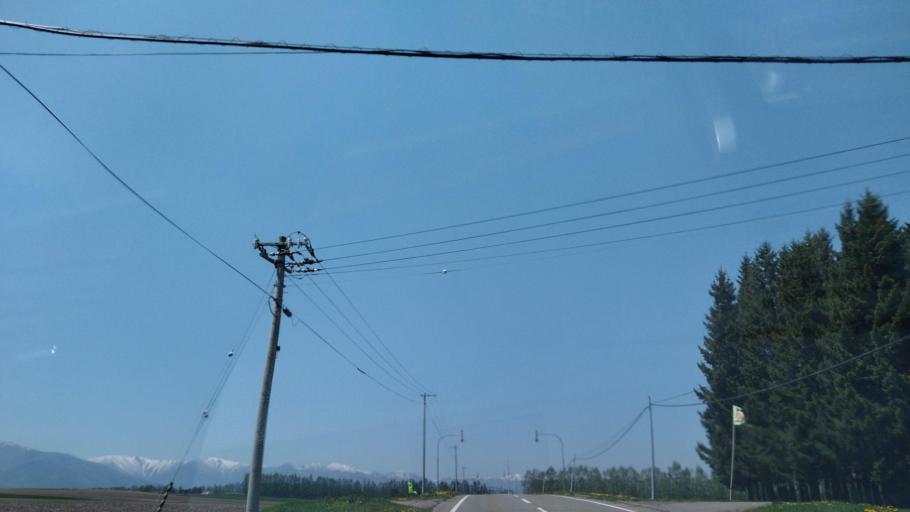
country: JP
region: Hokkaido
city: Obihiro
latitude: 42.9044
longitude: 143.0011
